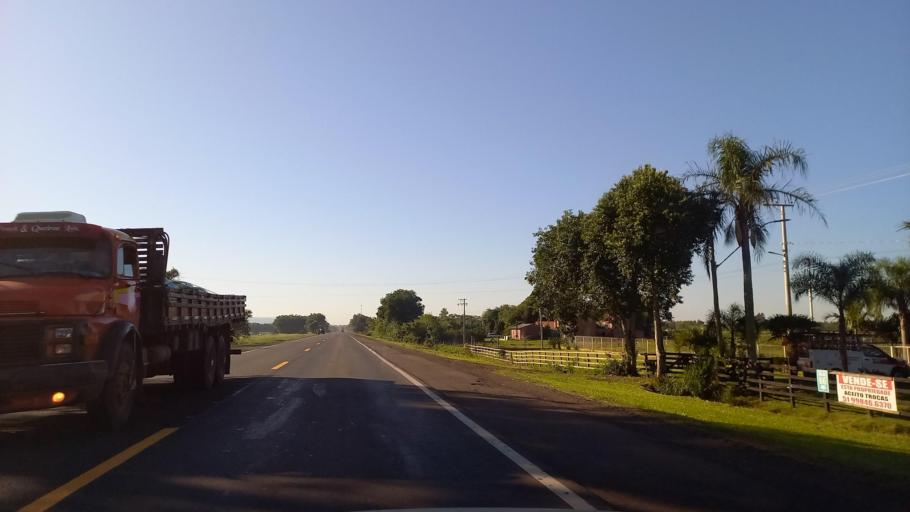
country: BR
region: Rio Grande do Sul
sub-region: Venancio Aires
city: Venancio Aires
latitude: -29.6610
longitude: -52.0694
